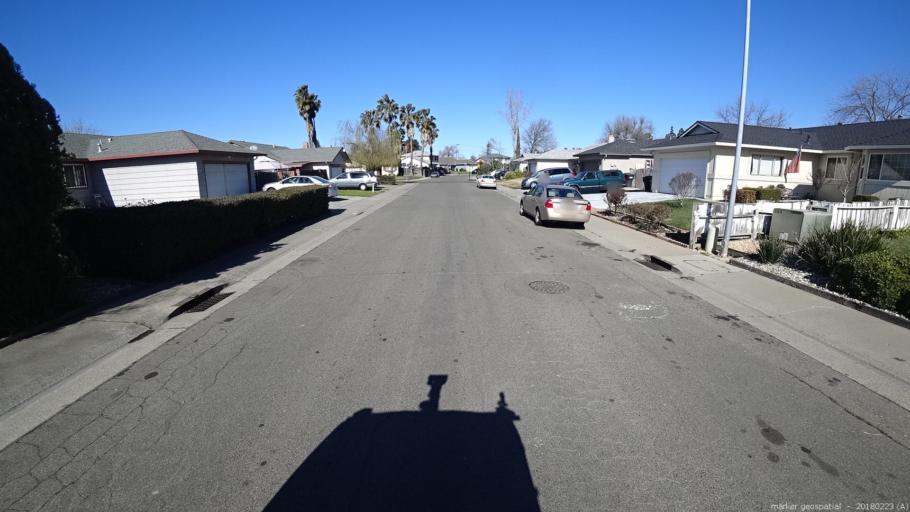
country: US
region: California
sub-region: Sacramento County
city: North Highlands
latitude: 38.7105
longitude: -121.3909
